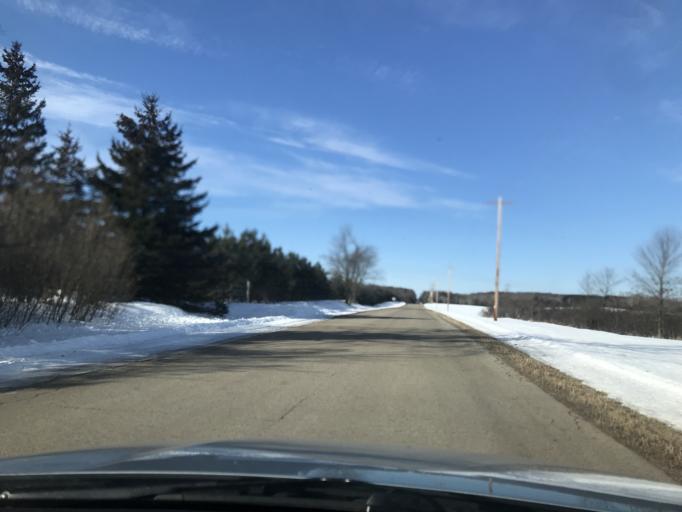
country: US
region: Wisconsin
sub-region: Oconto County
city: Gillett
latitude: 44.9614
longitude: -88.2669
